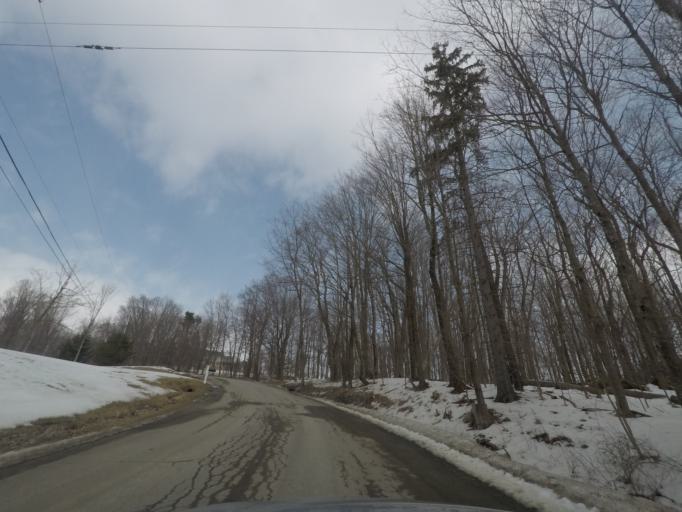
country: US
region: New York
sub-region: Saratoga County
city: Waterford
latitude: 42.7732
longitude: -73.6059
